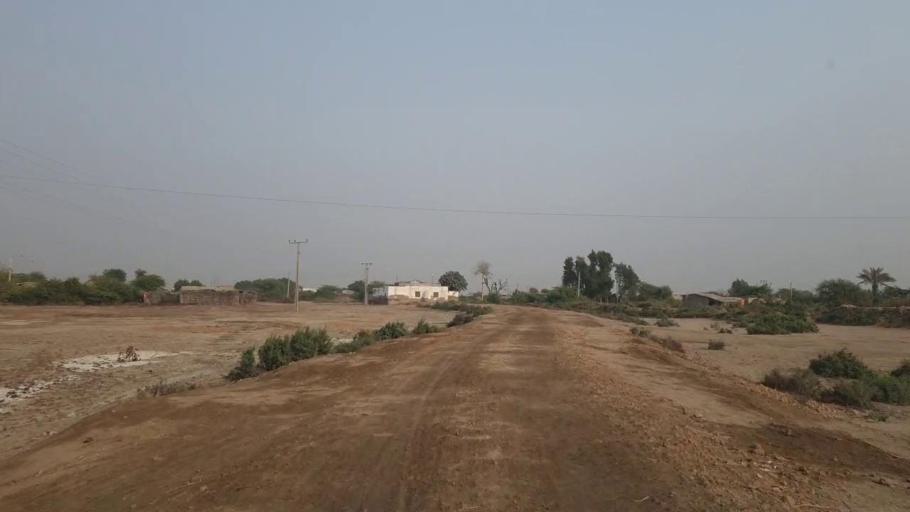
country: PK
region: Sindh
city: Mirpur Batoro
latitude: 24.5566
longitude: 68.4219
